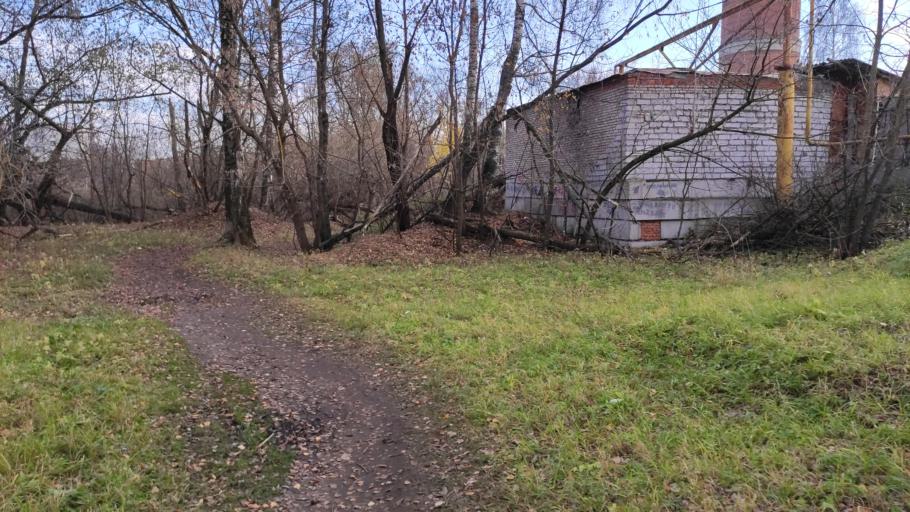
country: RU
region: Moskovskaya
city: Noginsk
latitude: 55.8734
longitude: 38.4586
